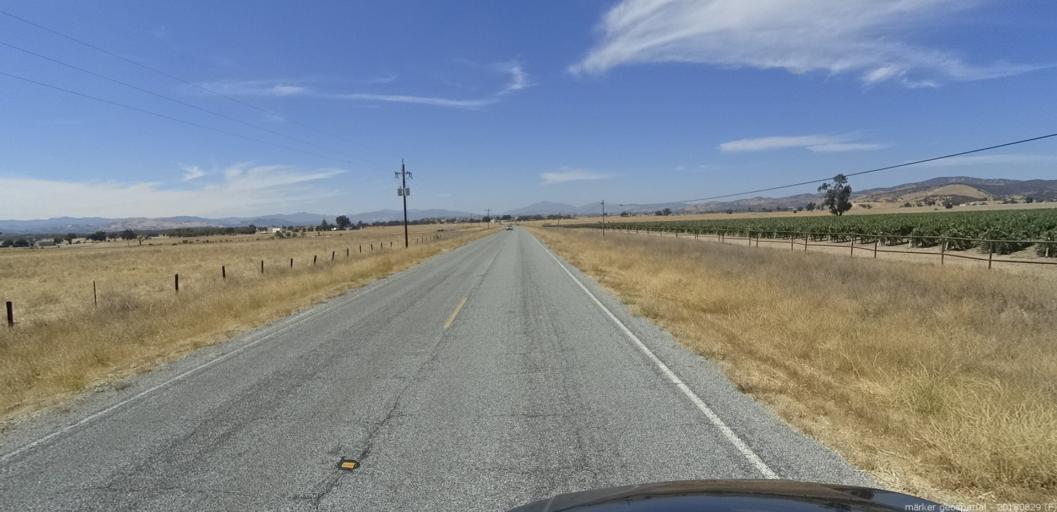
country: US
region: California
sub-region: San Luis Obispo County
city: Lake Nacimiento
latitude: 35.9342
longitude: -121.0594
